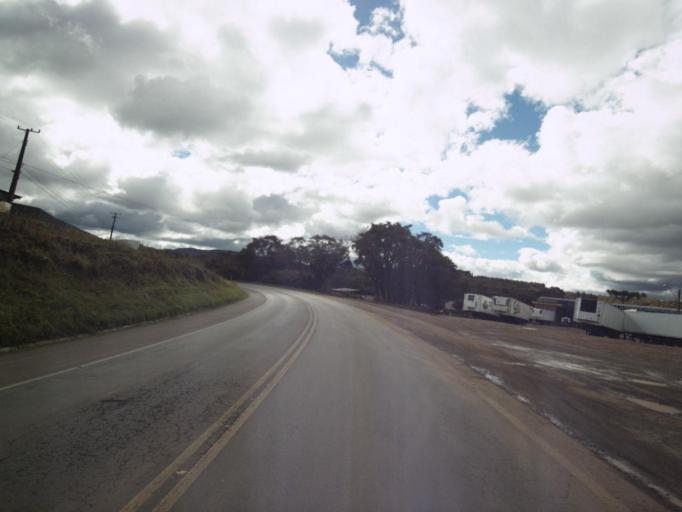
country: BR
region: Santa Catarina
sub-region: Concordia
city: Concordia
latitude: -27.2345
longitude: -51.9499
